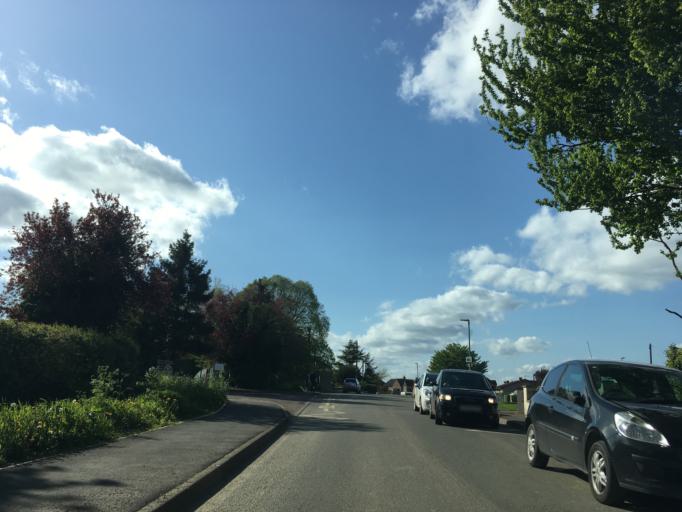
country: GB
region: England
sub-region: Gloucestershire
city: Stonehouse
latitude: 51.7310
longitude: -2.2789
